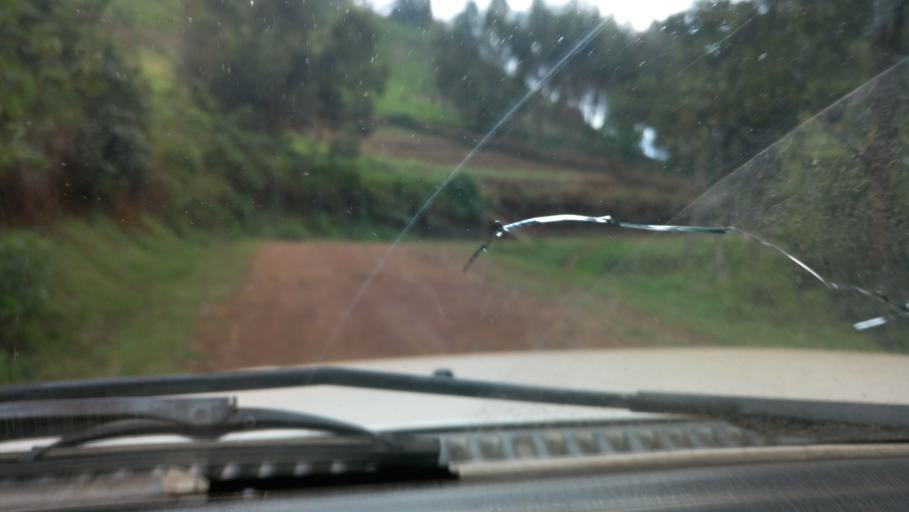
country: KE
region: Nyeri
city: Othaya
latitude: -0.6232
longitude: 36.8384
